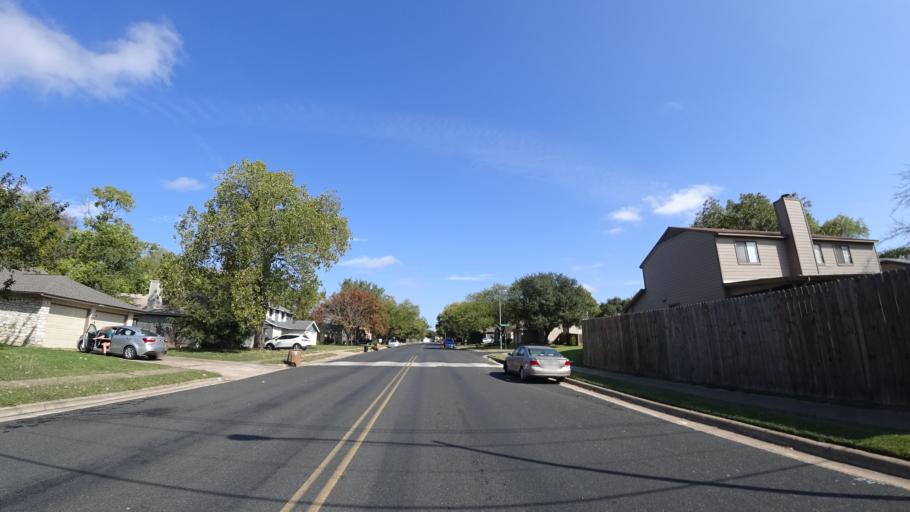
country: US
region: Texas
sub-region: Travis County
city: Shady Hollow
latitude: 30.1965
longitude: -97.8209
